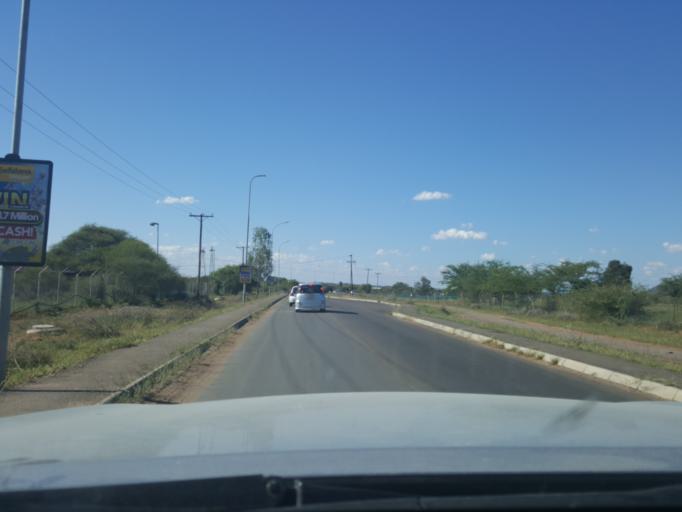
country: BW
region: South East
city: Gaborone
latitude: -24.6105
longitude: 25.9524
